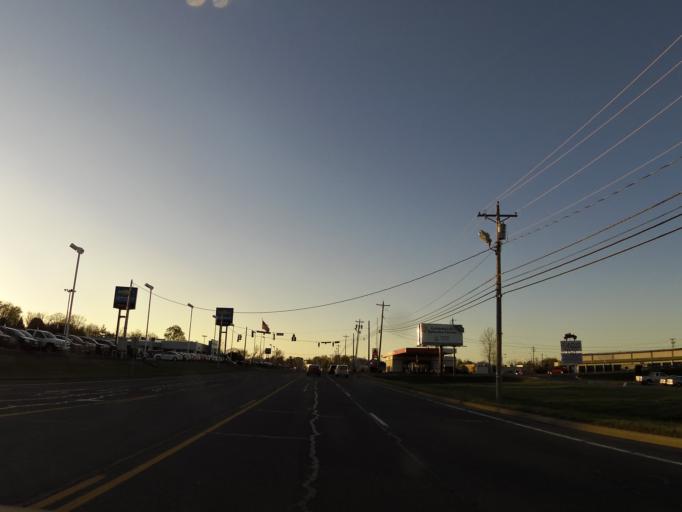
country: US
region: Tennessee
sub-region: Robertson County
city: Springfield
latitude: 36.4838
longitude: -86.8613
